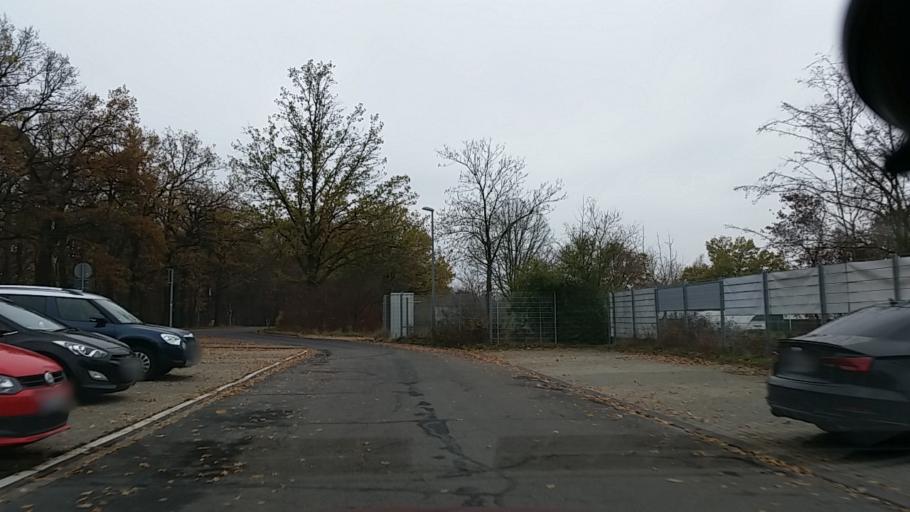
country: DE
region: Lower Saxony
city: Wolfsburg
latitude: 52.4520
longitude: 10.7946
